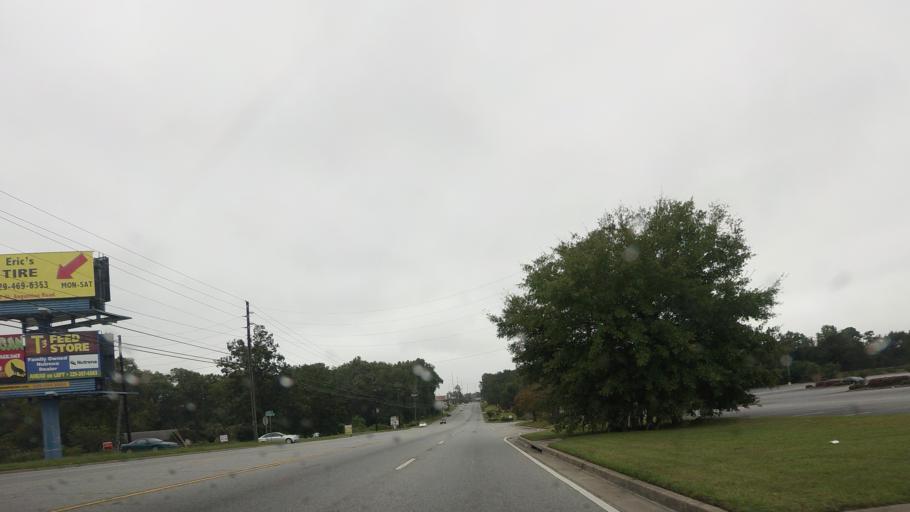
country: US
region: Georgia
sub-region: Lowndes County
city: Remerton
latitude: 30.8380
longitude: -83.3171
